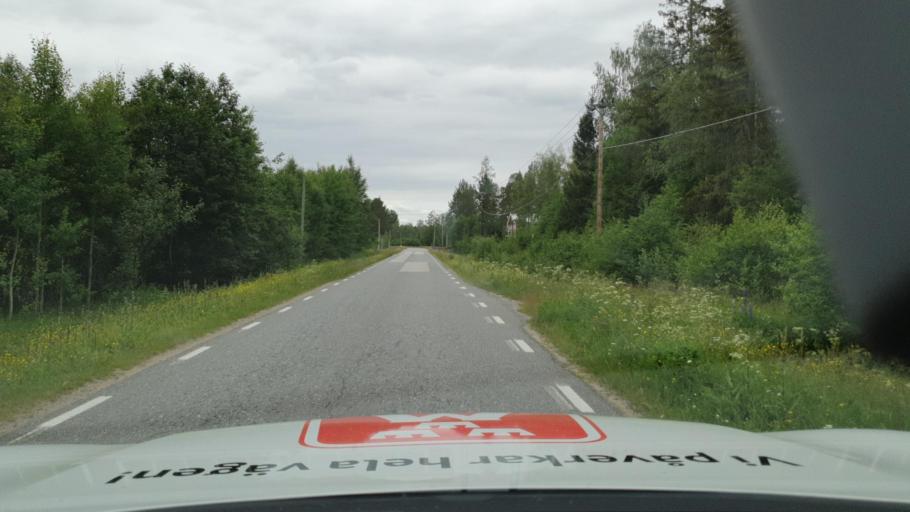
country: SE
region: Vaesterbotten
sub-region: Nordmalings Kommun
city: Nordmaling
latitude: 63.5242
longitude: 19.4157
